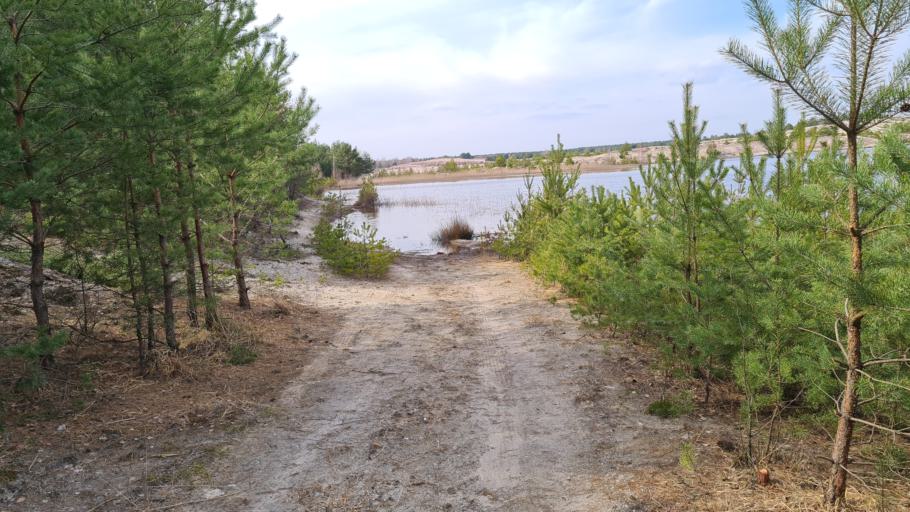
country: DE
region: Brandenburg
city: Lauchhammer
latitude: 51.5412
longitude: 13.7159
